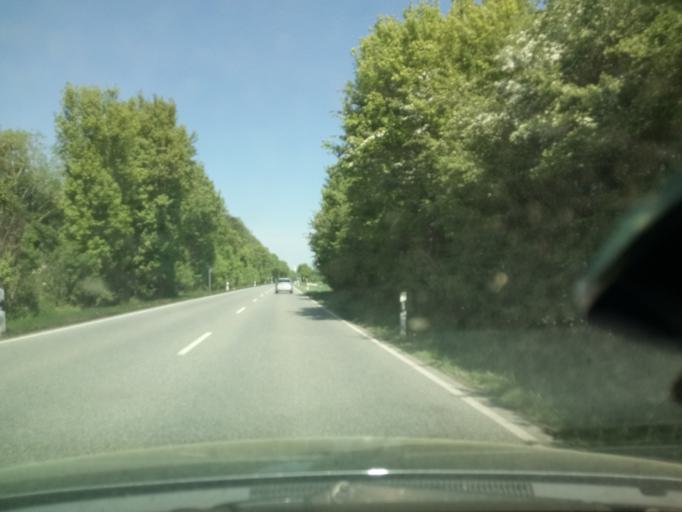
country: DE
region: Bavaria
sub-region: Upper Bavaria
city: Altoetting
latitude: 48.2244
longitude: 12.6921
